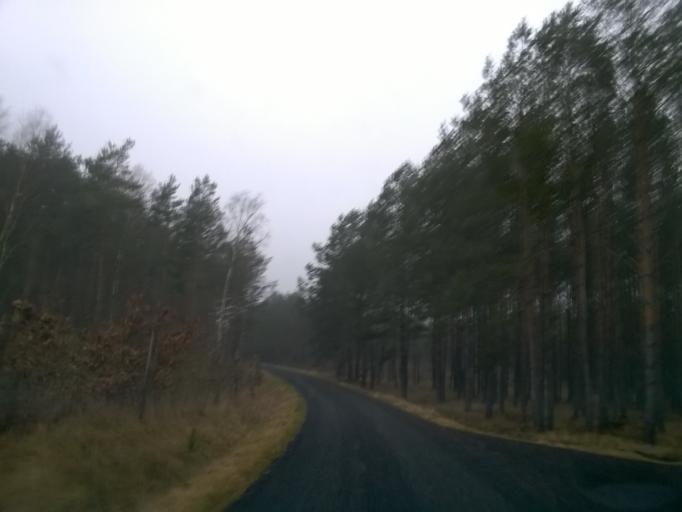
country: PL
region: Kujawsko-Pomorskie
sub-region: Powiat nakielski
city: Kcynia
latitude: 53.0557
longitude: 17.4447
